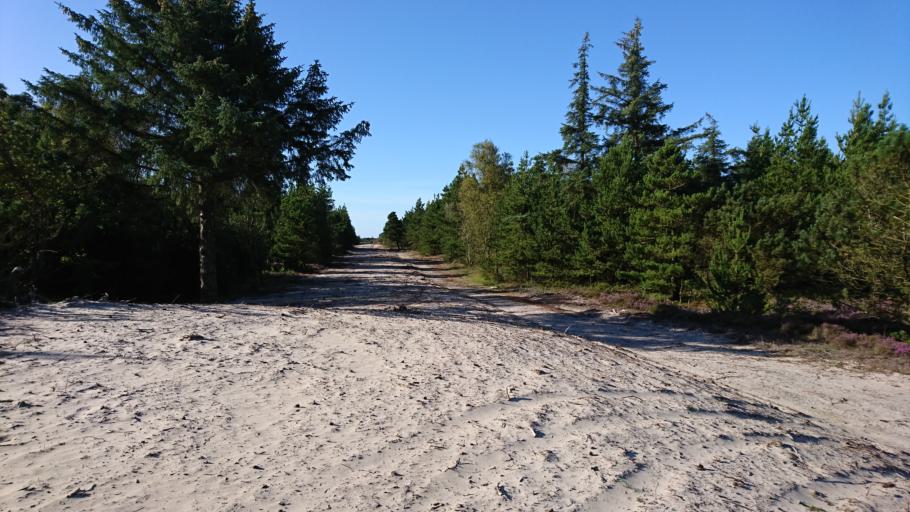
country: DK
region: South Denmark
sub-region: Fano Kommune
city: Nordby
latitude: 55.3955
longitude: 8.4231
